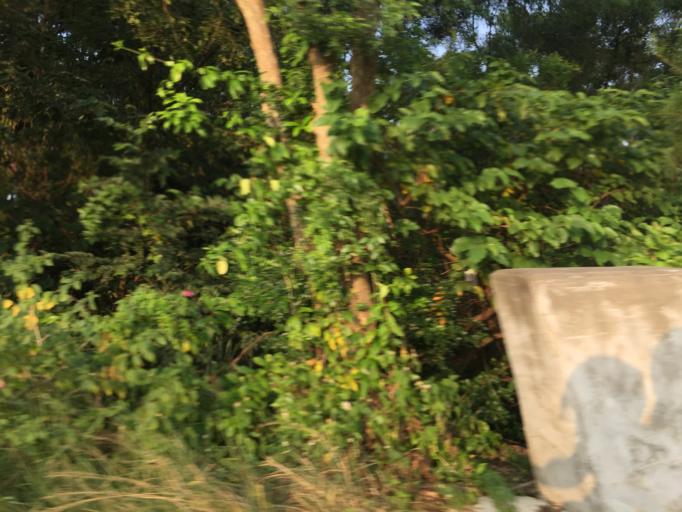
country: TW
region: Taiwan
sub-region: Hsinchu
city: Hsinchu
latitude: 24.7861
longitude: 120.9503
